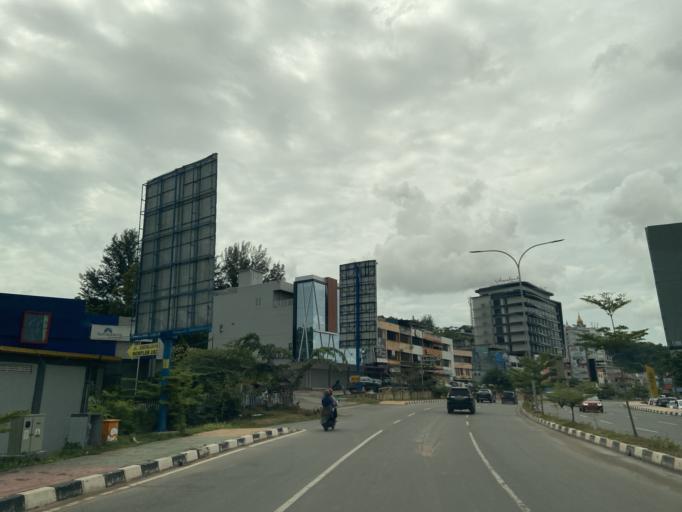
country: SG
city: Singapore
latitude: 1.1450
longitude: 104.0179
